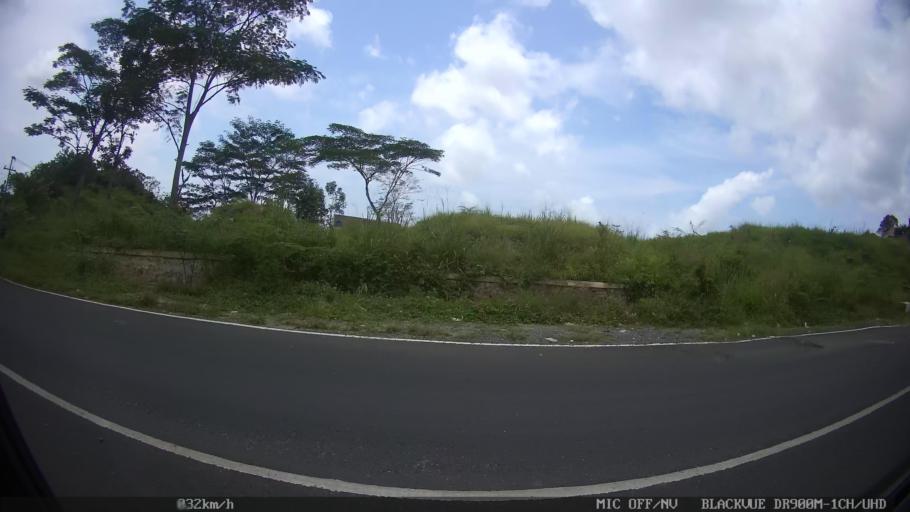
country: ID
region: Lampung
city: Bandarlampung
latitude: -5.4121
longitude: 105.2372
